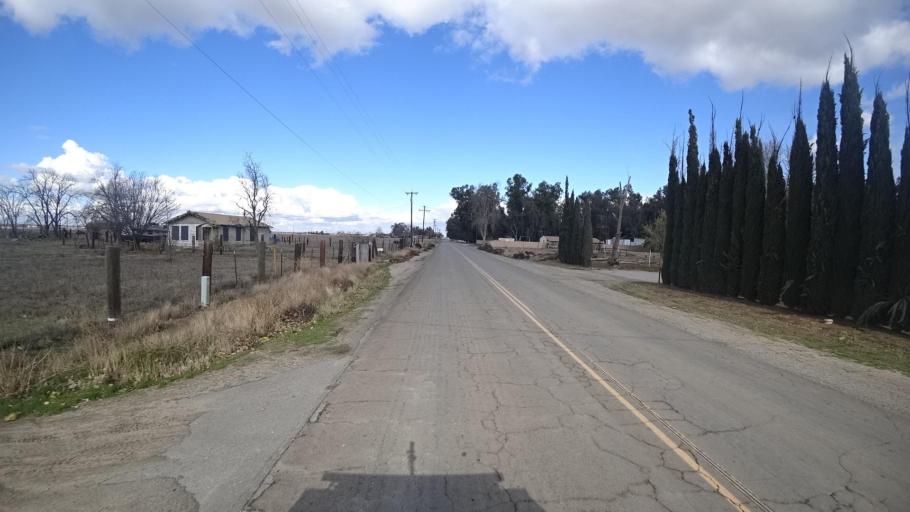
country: US
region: California
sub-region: Kern County
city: Greenfield
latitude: 35.2299
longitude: -119.0922
